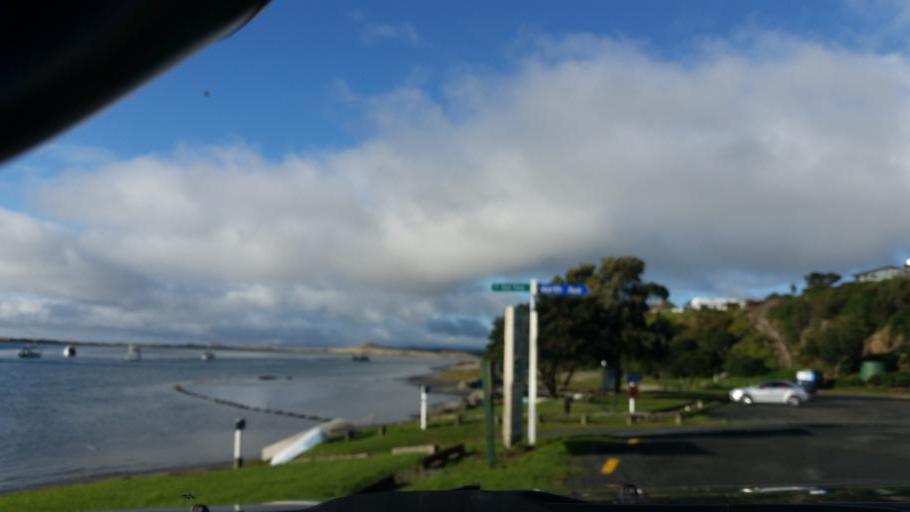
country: NZ
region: Auckland
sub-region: Auckland
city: Wellsford
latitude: -36.0901
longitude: 174.5900
